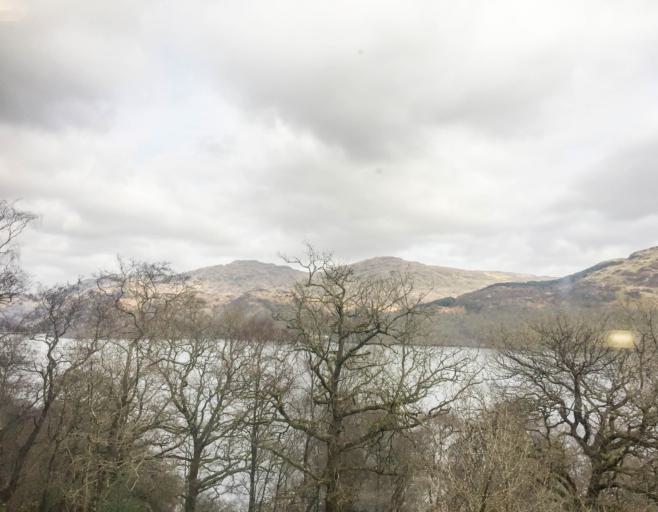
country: GB
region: Scotland
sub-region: Argyll and Bute
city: Garelochhead
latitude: 56.2282
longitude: -4.7011
